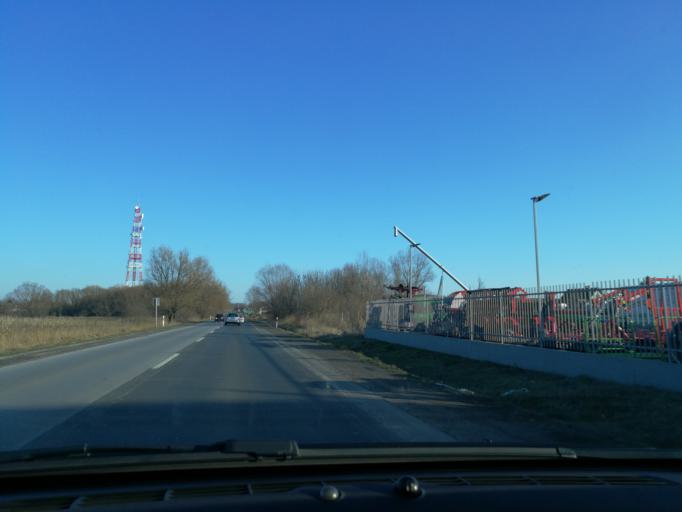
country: HU
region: Szabolcs-Szatmar-Bereg
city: Nyirpazony
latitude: 47.9489
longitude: 21.7928
